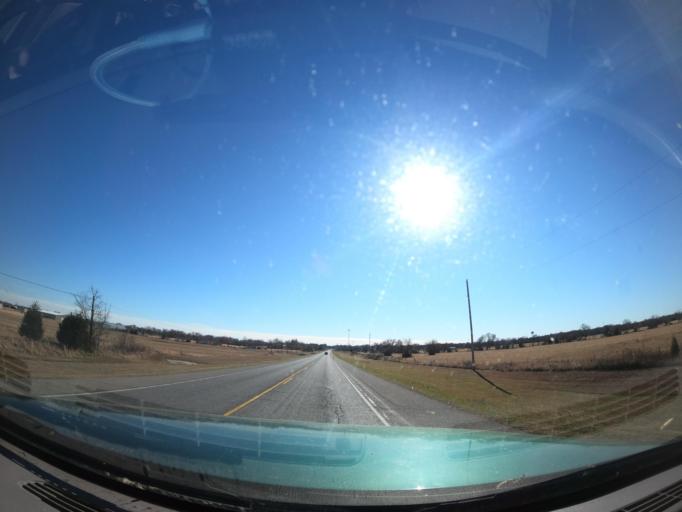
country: US
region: Oklahoma
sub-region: Muskogee County
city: Haskell
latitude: 35.8334
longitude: -95.6776
